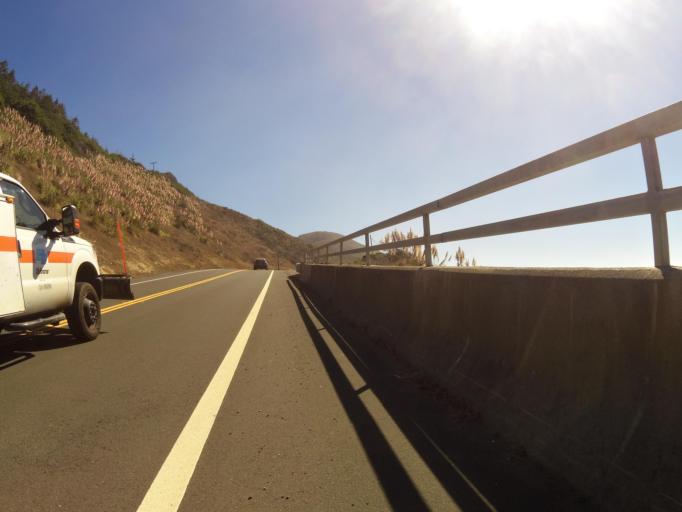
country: US
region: California
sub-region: Mendocino County
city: Fort Bragg
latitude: 39.6105
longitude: -123.7826
